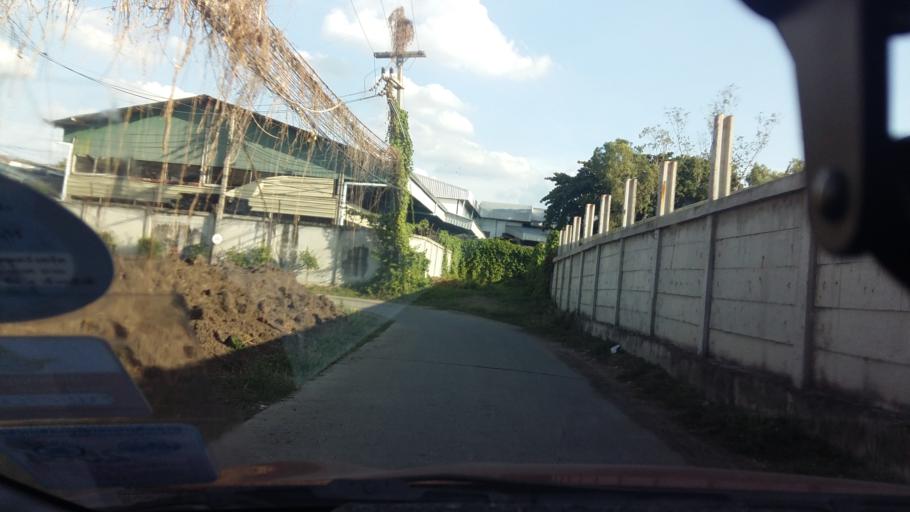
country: TH
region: Lop Buri
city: Lop Buri
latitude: 14.8299
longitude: 100.6486
